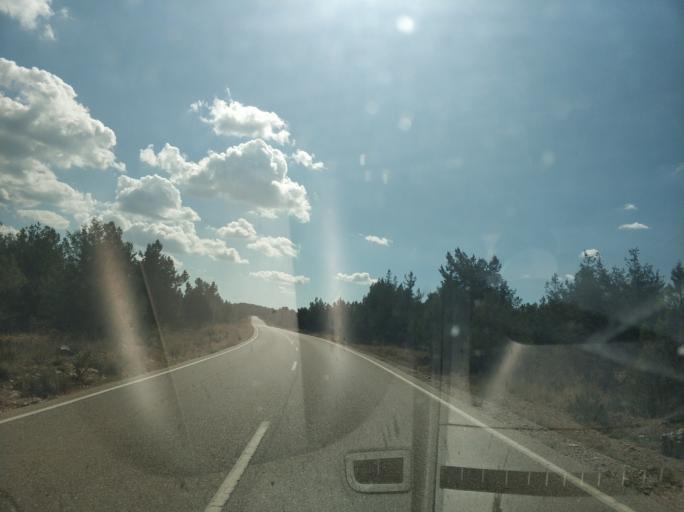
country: ES
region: Castille and Leon
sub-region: Provincia de Soria
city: Ucero
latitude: 41.7393
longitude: -3.0446
